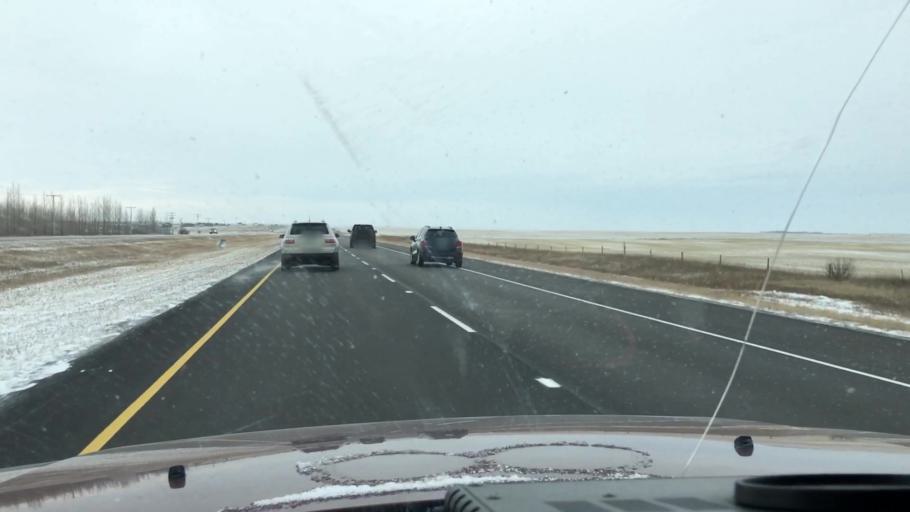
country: CA
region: Saskatchewan
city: Saskatoon
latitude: 51.7693
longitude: -106.4763
